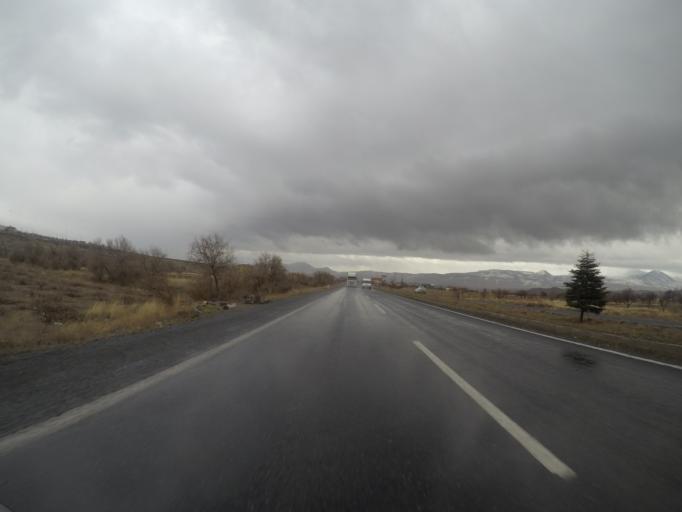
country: TR
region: Kayseri
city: Incesu
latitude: 38.6810
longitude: 35.2141
